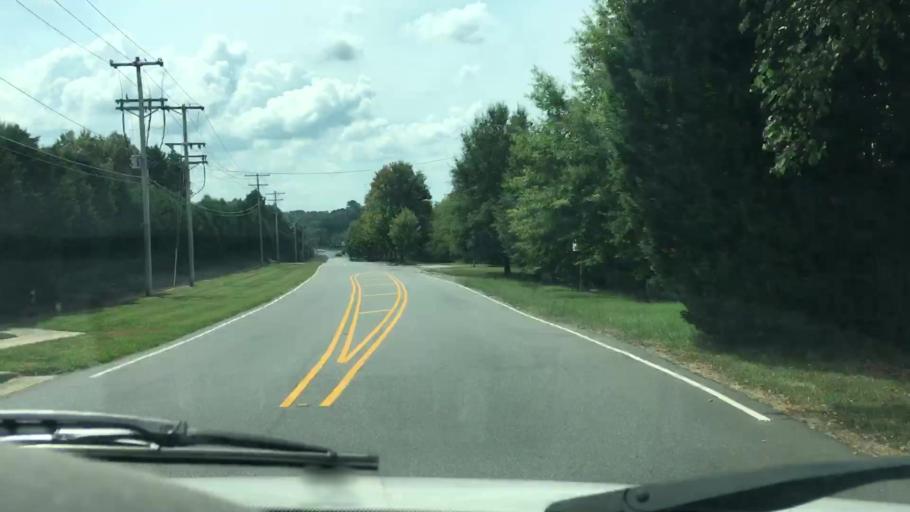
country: US
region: North Carolina
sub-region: Mecklenburg County
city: Cornelius
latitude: 35.4481
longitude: -80.8727
